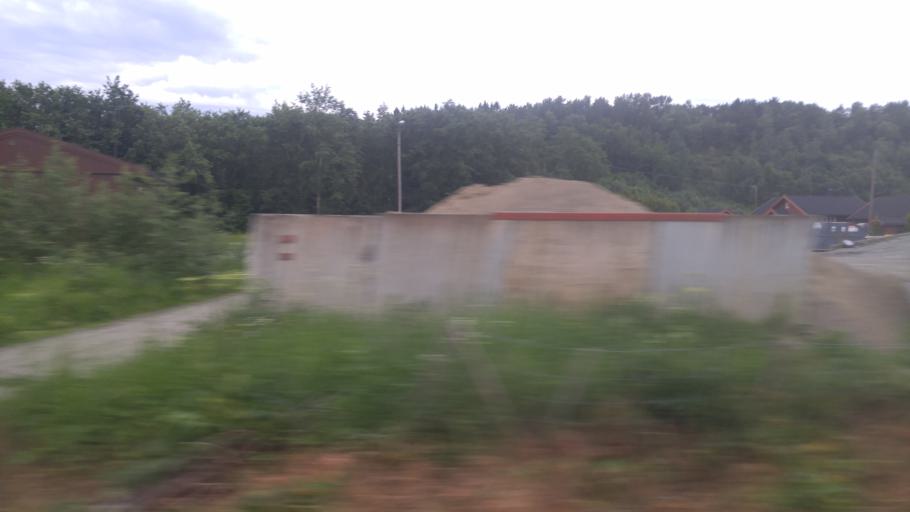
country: NO
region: Nord-Trondelag
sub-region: Stjordal
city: Stjordalshalsen
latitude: 63.4480
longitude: 10.9538
